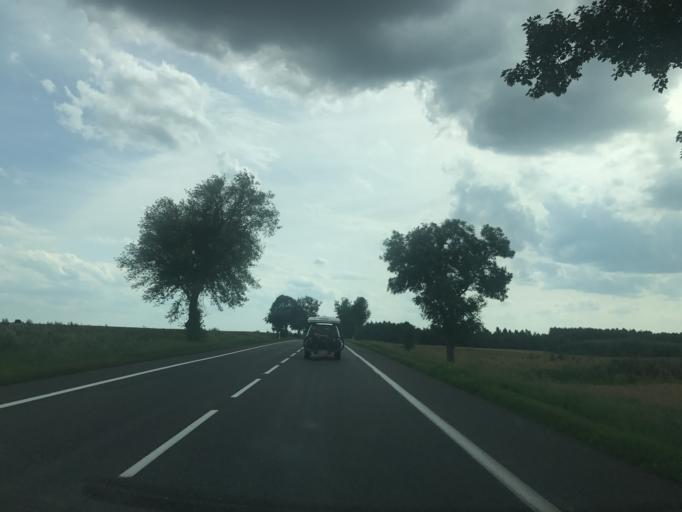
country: PL
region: Masovian Voivodeship
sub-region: Powiat mlawski
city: Wisniewo
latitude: 53.0186
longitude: 20.3341
